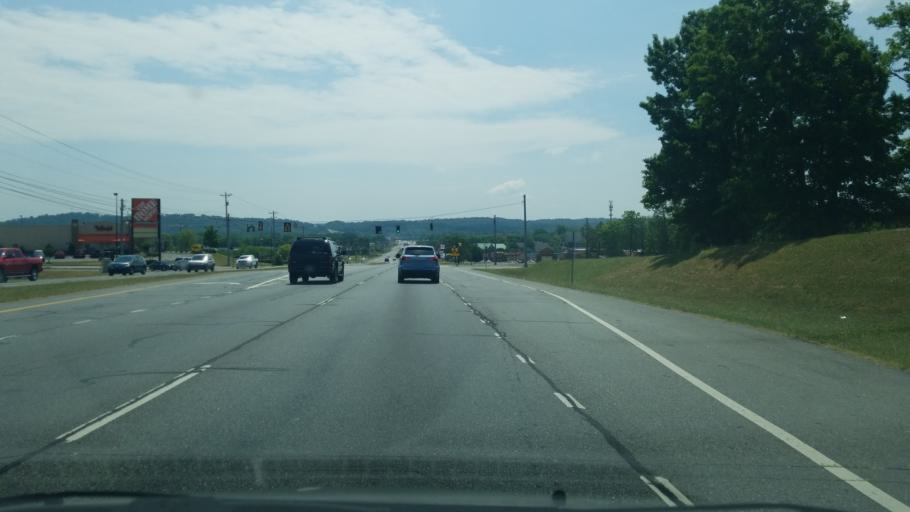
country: US
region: Georgia
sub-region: Catoosa County
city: Fort Oglethorpe
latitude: 34.9470
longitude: -85.2324
